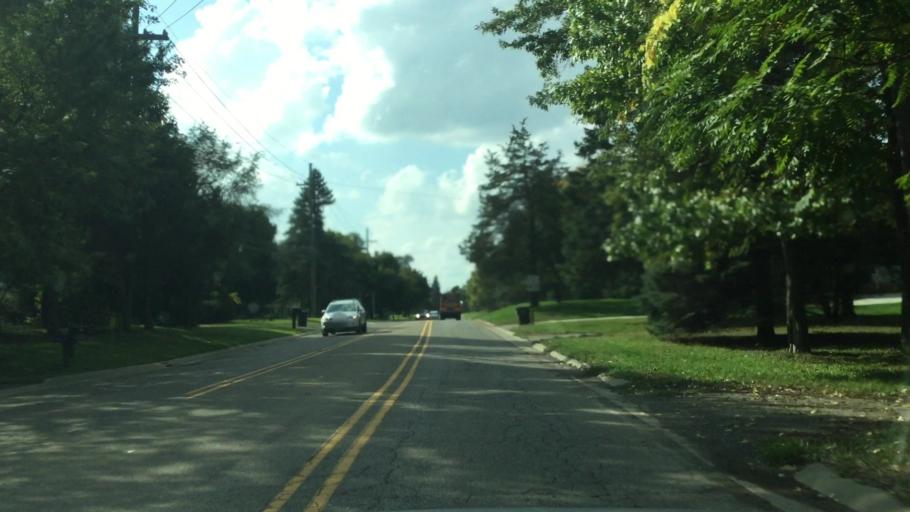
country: US
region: Michigan
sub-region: Oakland County
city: Waterford
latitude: 42.6521
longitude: -83.4261
